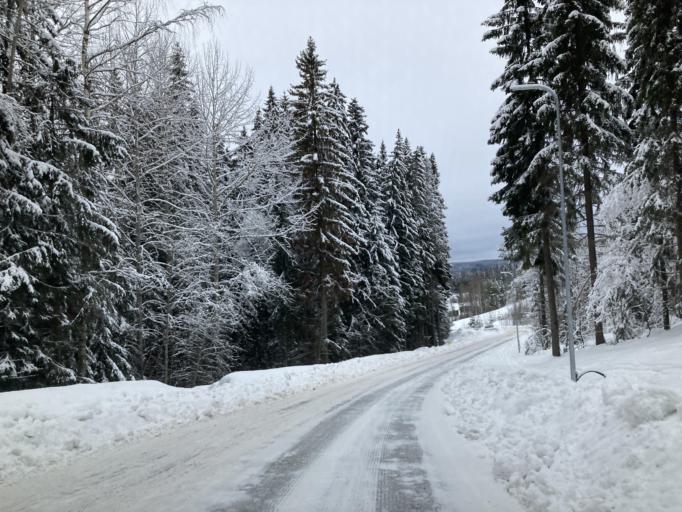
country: FI
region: Central Finland
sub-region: Jaemsae
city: Jaemsae
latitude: 61.8786
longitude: 25.3069
